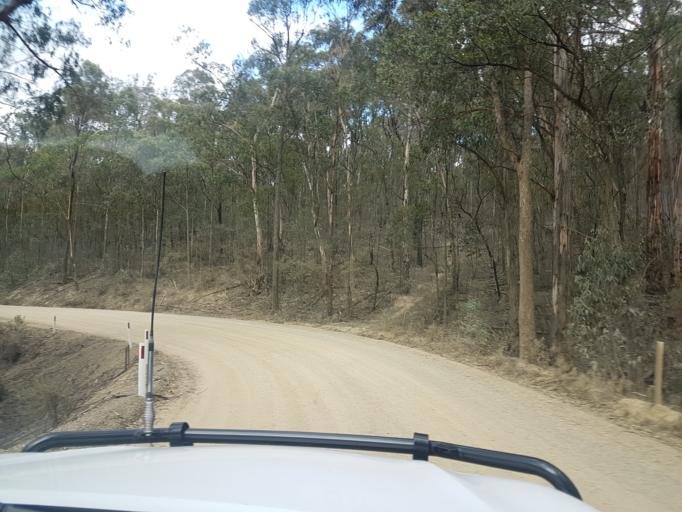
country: AU
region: Victoria
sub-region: East Gippsland
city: Bairnsdale
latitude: -37.6965
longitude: 147.5650
